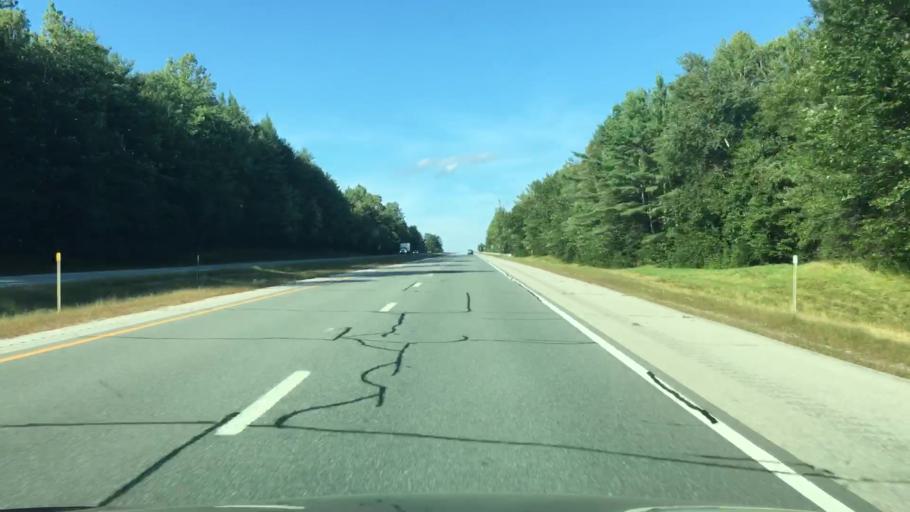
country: US
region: New Hampshire
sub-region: Grafton County
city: Littleton
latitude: 44.2527
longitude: -71.7592
